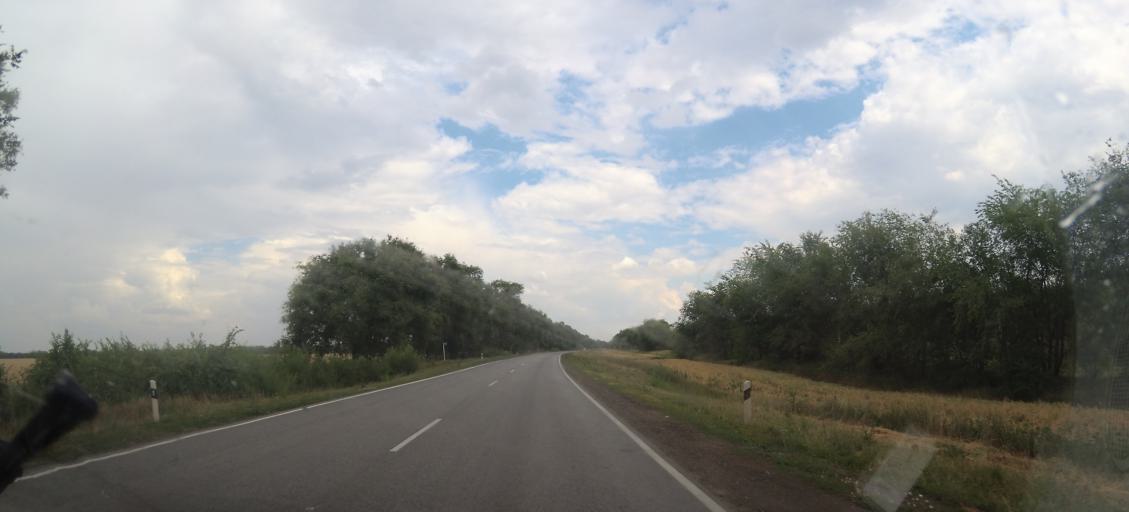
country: RU
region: Rostov
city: Peschanokopskoye
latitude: 46.2038
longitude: 41.2020
